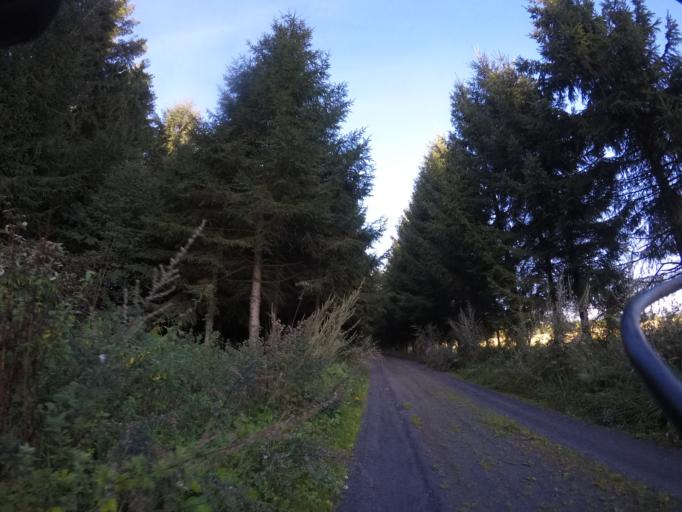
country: BE
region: Wallonia
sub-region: Province du Luxembourg
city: Bastogne
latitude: 49.9752
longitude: 5.6961
